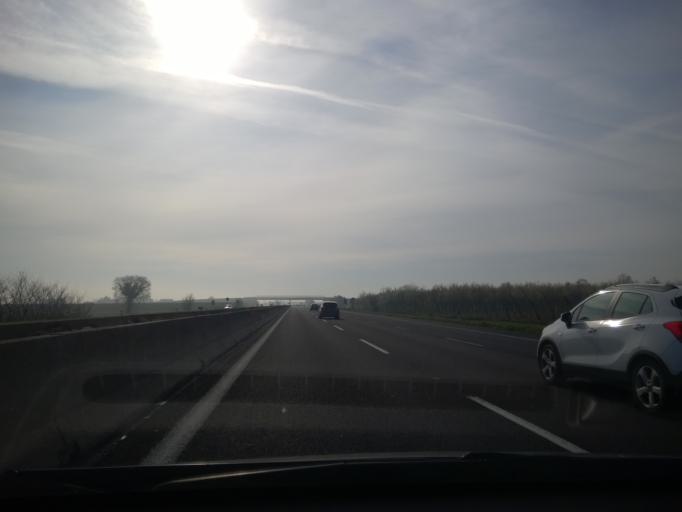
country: IT
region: Emilia-Romagna
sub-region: Provincia di Bologna
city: Castel Guelfo di Bologna
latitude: 44.4076
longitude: 11.6718
